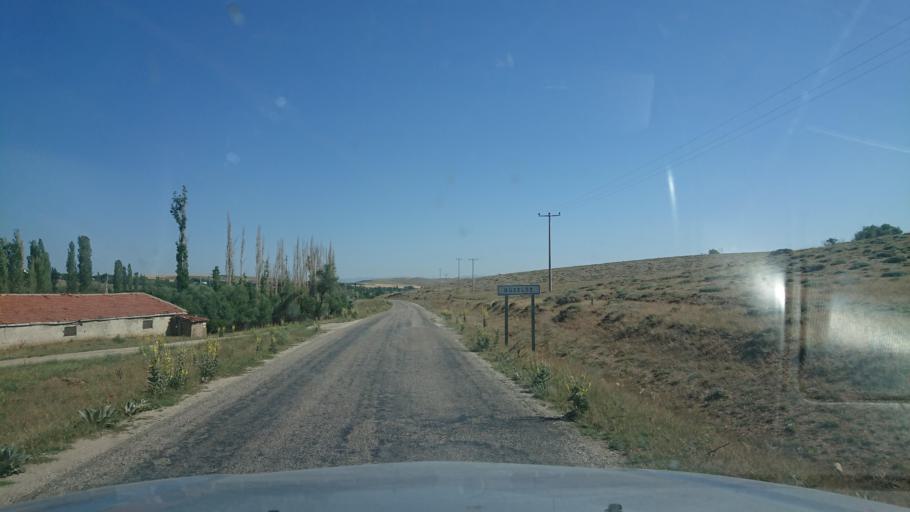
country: TR
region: Aksaray
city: Agacoren
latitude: 38.8745
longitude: 33.8805
